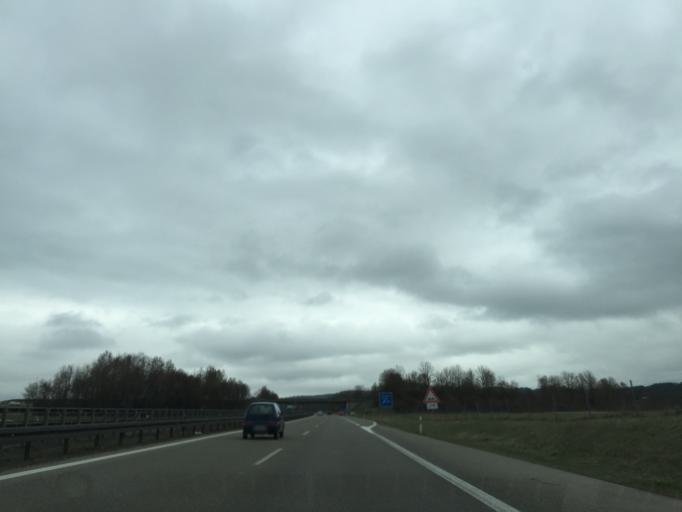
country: DE
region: Baden-Wuerttemberg
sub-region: Freiburg Region
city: Bad Durrheim
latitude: 47.9889
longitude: 8.5250
